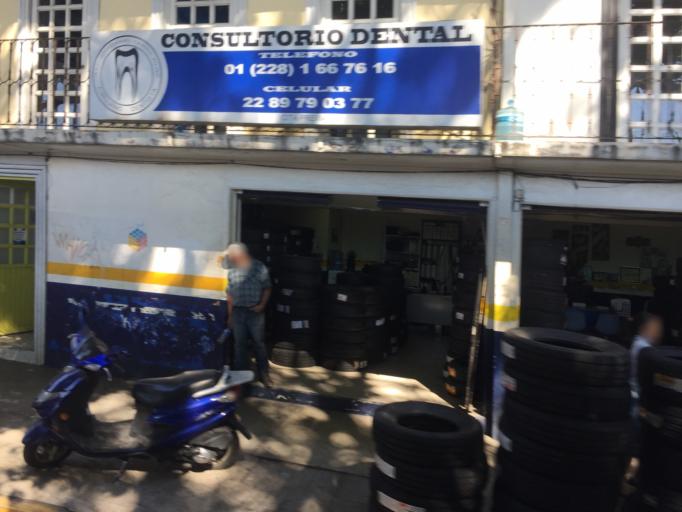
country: MX
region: Veracruz
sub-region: Xalapa
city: Xalapa de Enriquez
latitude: 19.5316
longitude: -96.9072
